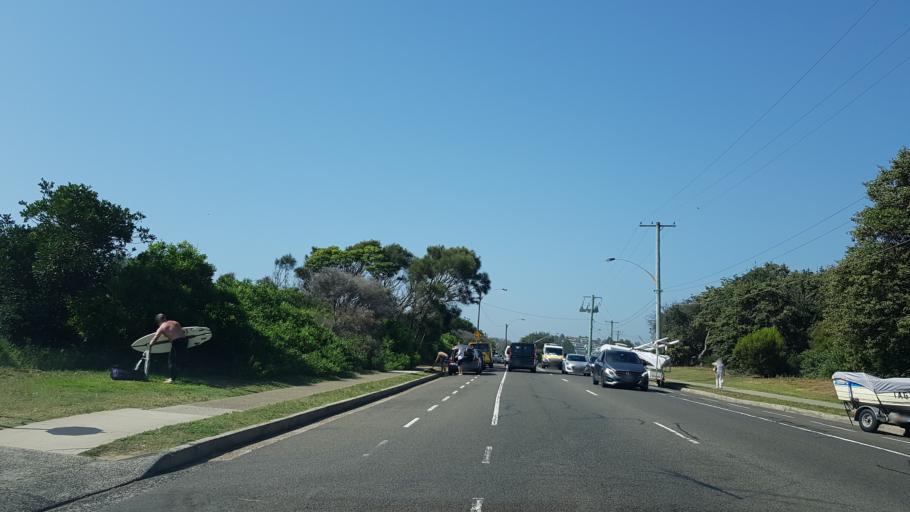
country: AU
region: New South Wales
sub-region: Warringah
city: Curl Curl
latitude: -33.7675
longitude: 151.2946
